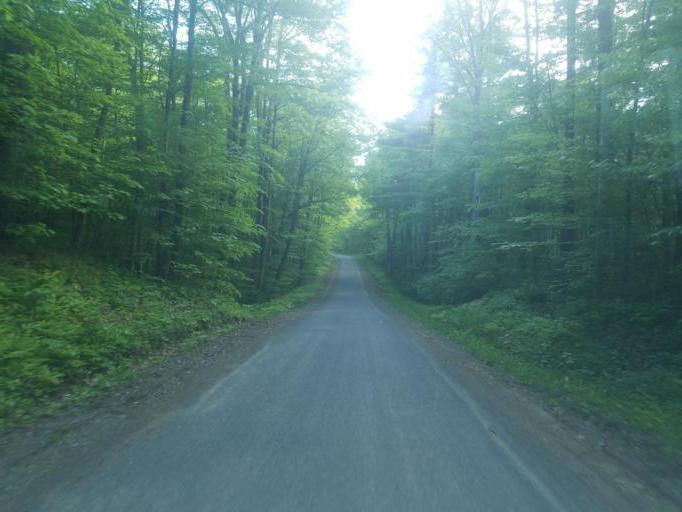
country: US
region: New York
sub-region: Herkimer County
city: Dolgeville
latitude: 43.3690
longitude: -74.9198
